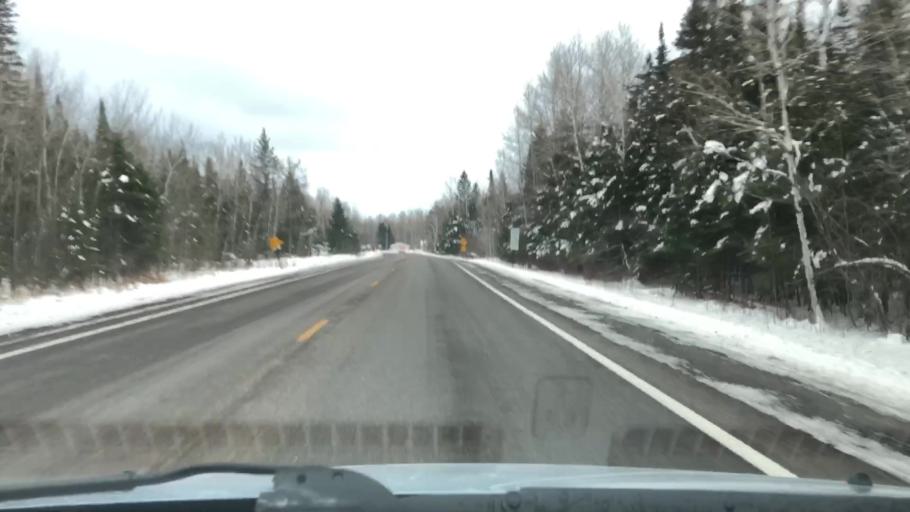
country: US
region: Minnesota
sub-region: Carlton County
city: Carlton
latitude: 46.6666
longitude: -92.3858
